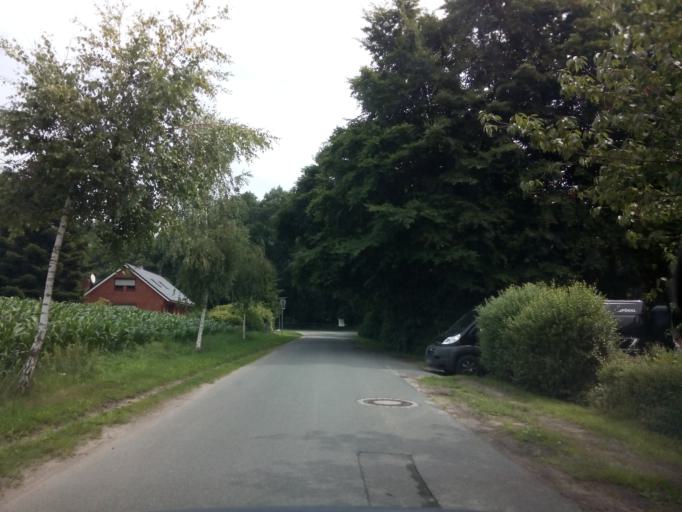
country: DE
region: Lower Saxony
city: Worpswede
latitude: 53.2134
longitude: 8.9126
